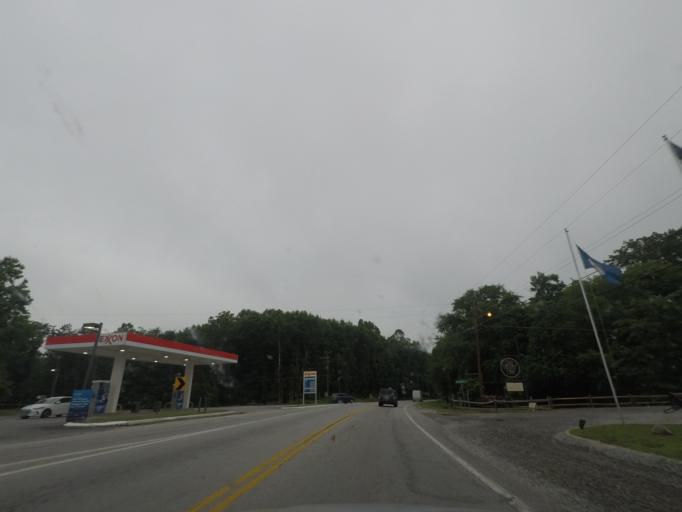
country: US
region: Virginia
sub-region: Prince Edward County
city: Hampden Sydney
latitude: 37.2463
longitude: -78.4437
